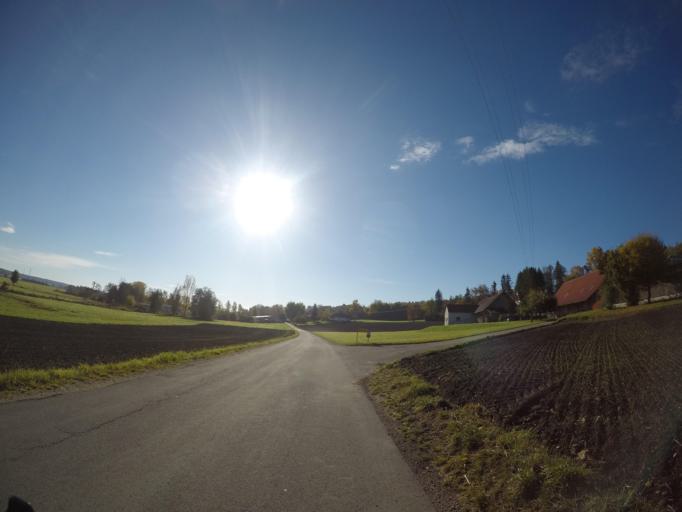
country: DE
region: Baden-Wuerttemberg
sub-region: Tuebingen Region
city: Saulgau
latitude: 48.0352
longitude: 9.4749
